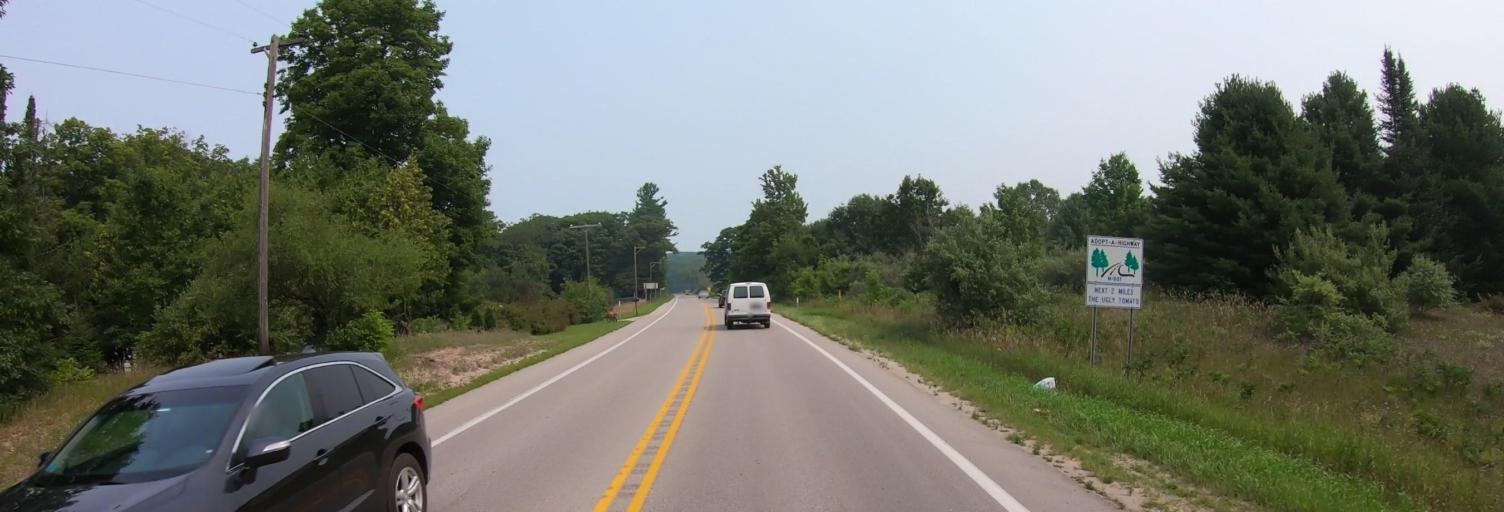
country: US
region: Michigan
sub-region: Leelanau County
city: Leland
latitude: 44.9449
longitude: -85.8018
